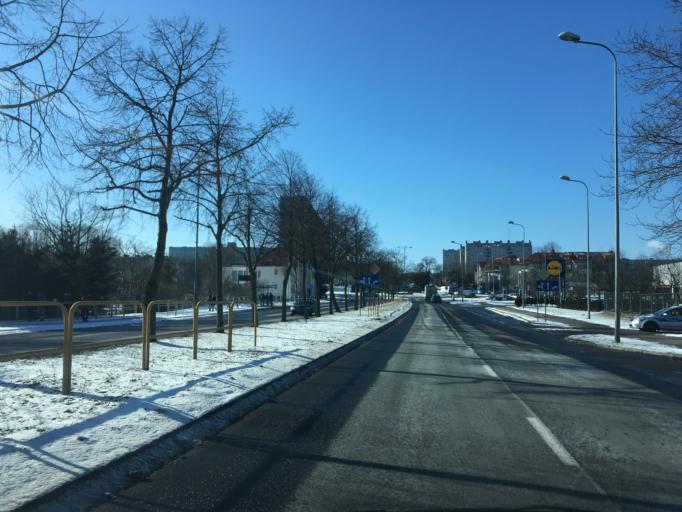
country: PL
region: Pomeranian Voivodeship
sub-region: Slupsk
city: Slupsk
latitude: 54.4729
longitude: 17.0159
